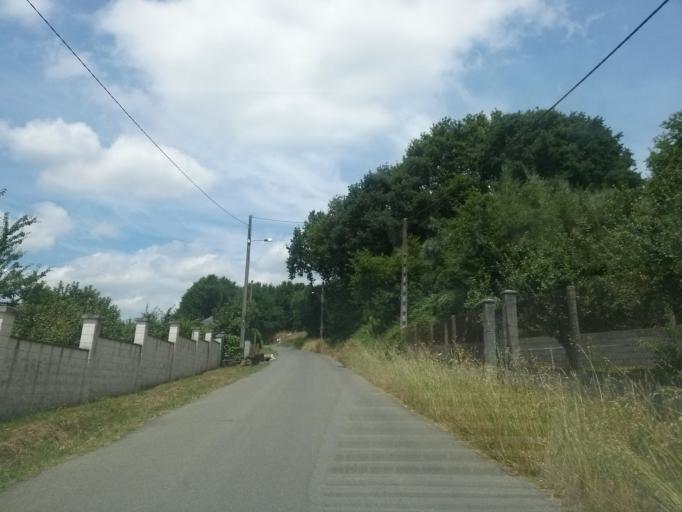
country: ES
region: Galicia
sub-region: Provincia de Lugo
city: Lugo
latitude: 43.0369
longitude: -7.5943
